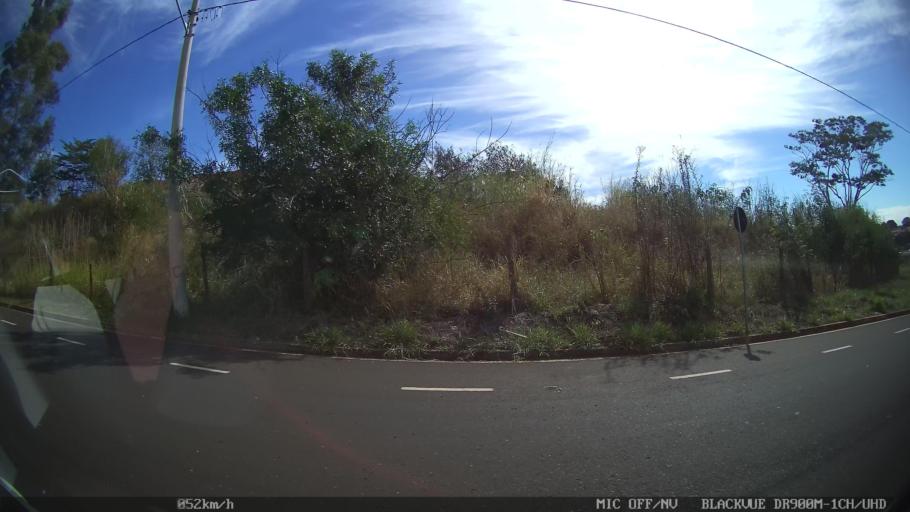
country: BR
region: Sao Paulo
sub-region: Sao Jose Do Rio Preto
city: Sao Jose do Rio Preto
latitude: -20.8494
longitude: -49.3745
